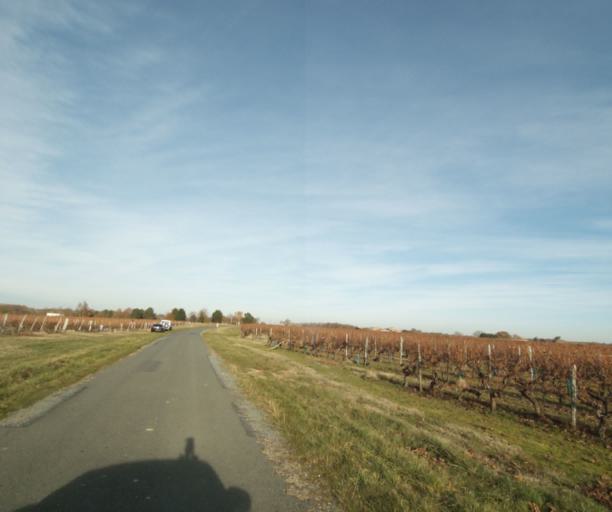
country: FR
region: Poitou-Charentes
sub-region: Departement de la Charente-Maritime
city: Chaniers
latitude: 45.7510
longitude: -0.5198
